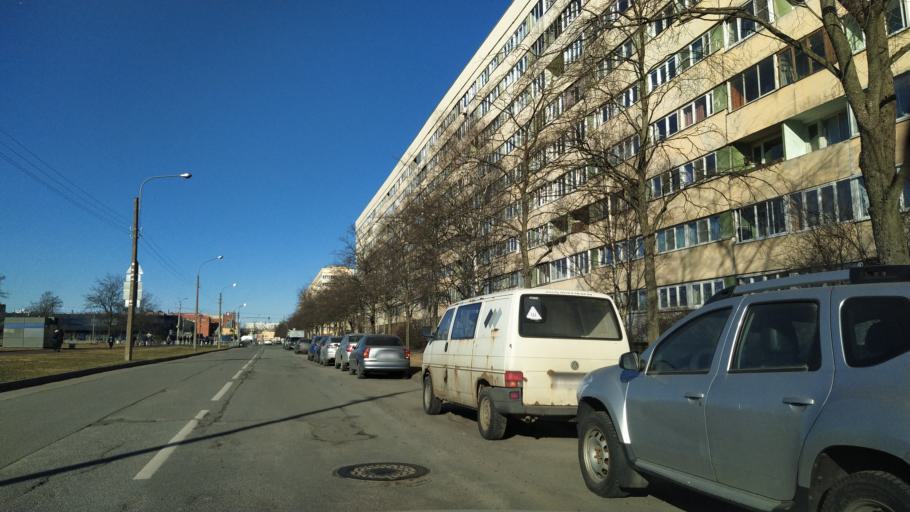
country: RU
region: St.-Petersburg
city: Grazhdanka
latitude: 60.0395
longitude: 30.3906
